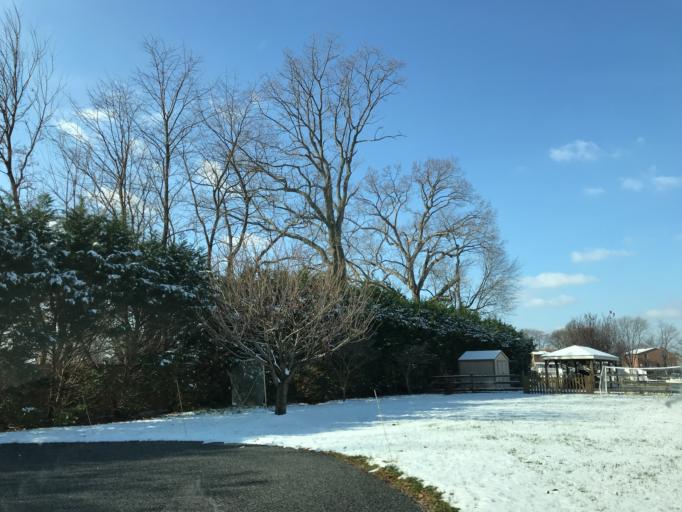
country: US
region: Maryland
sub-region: Baltimore County
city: Bowleys Quarters
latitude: 39.3300
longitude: -76.3998
